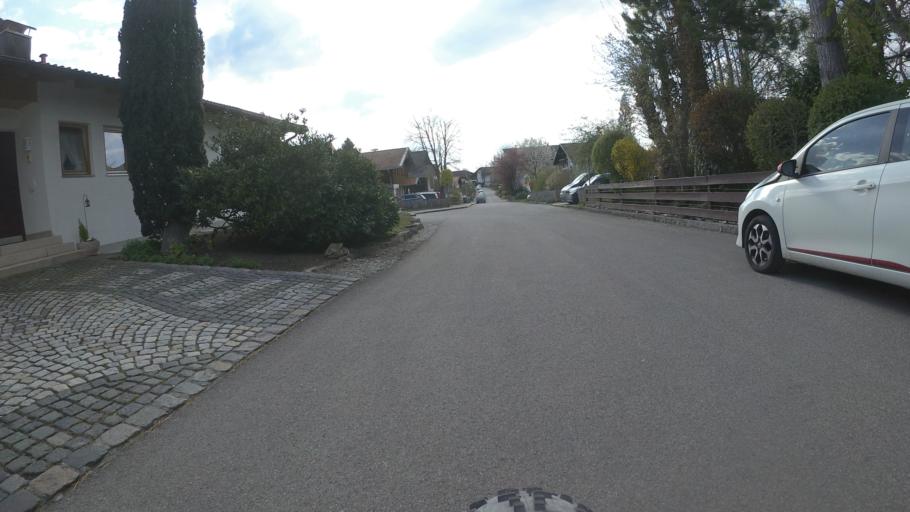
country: DE
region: Bavaria
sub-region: Upper Bavaria
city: Seeon-Seebruck
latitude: 47.9371
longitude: 12.4763
